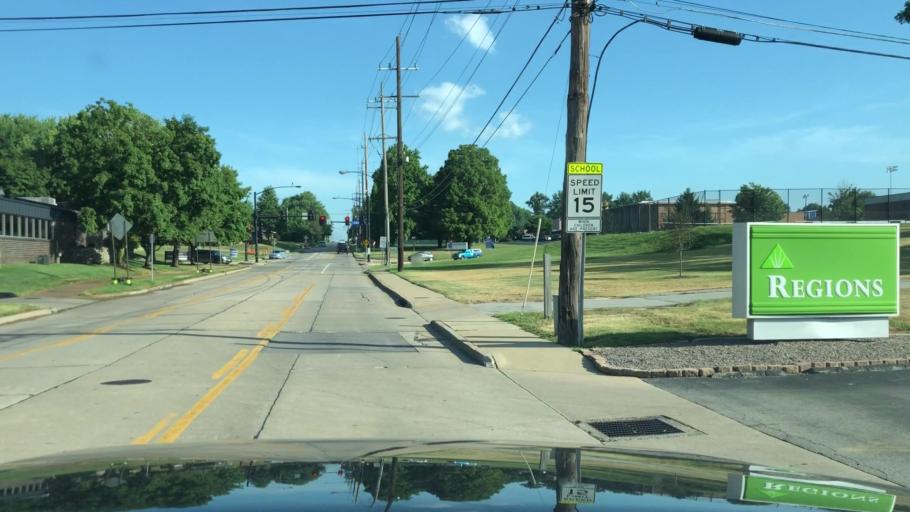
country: US
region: Missouri
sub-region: Saint Charles County
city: Saint Charles
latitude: 38.7951
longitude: -90.4995
